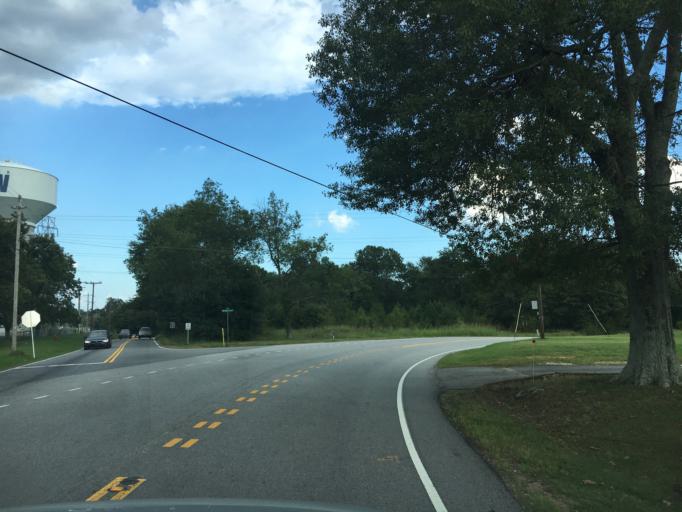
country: US
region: South Carolina
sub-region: Greenville County
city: Greer
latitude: 34.9064
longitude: -82.2311
